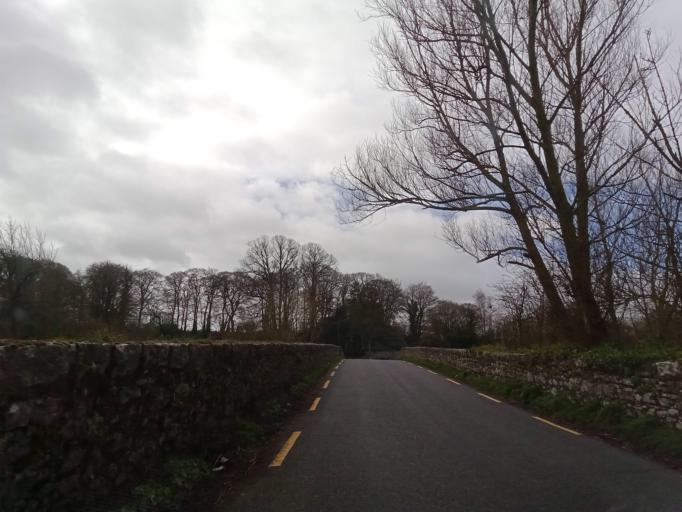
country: IE
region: Leinster
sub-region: Kilkenny
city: Ballyragget
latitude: 52.7141
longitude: -7.3225
